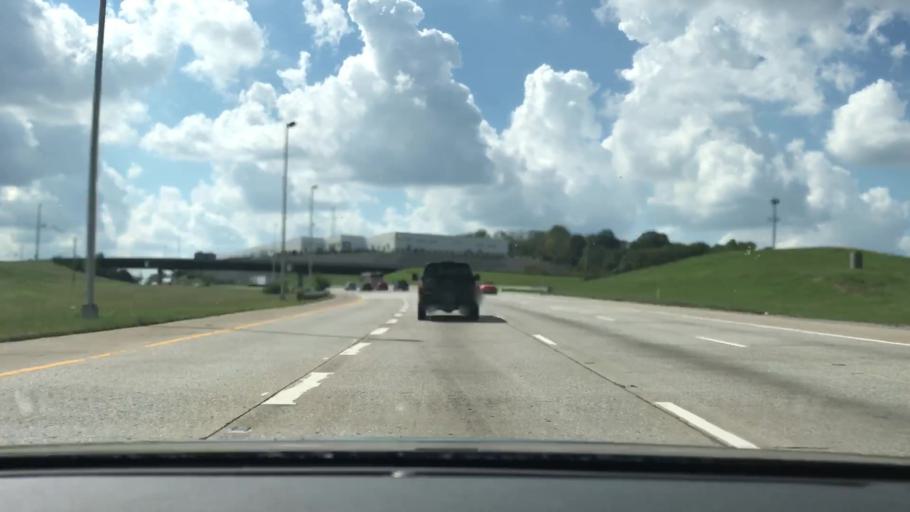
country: US
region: Tennessee
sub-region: Davidson County
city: Nashville
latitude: 36.2271
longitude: -86.7737
